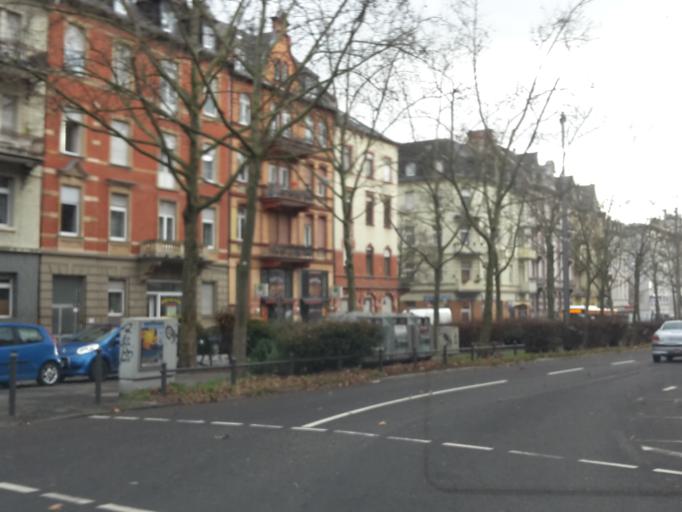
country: DE
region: Hesse
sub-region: Regierungsbezirk Darmstadt
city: Wiesbaden
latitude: 50.0825
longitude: 8.2291
